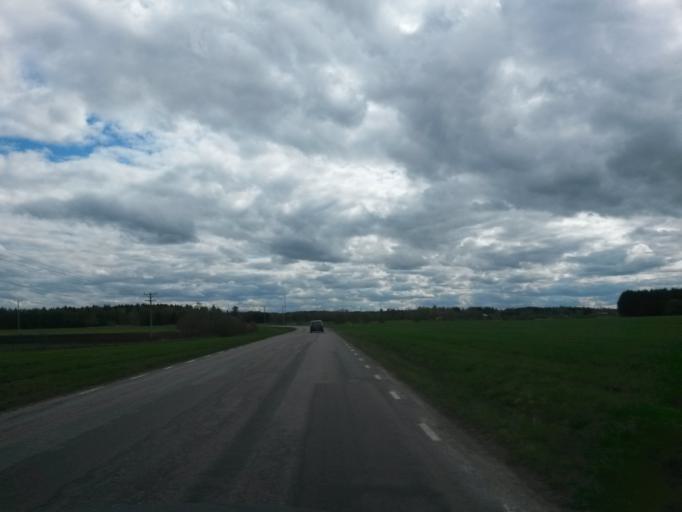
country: SE
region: Vaestra Goetaland
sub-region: Essunga Kommun
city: Nossebro
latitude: 58.1628
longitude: 12.7454
